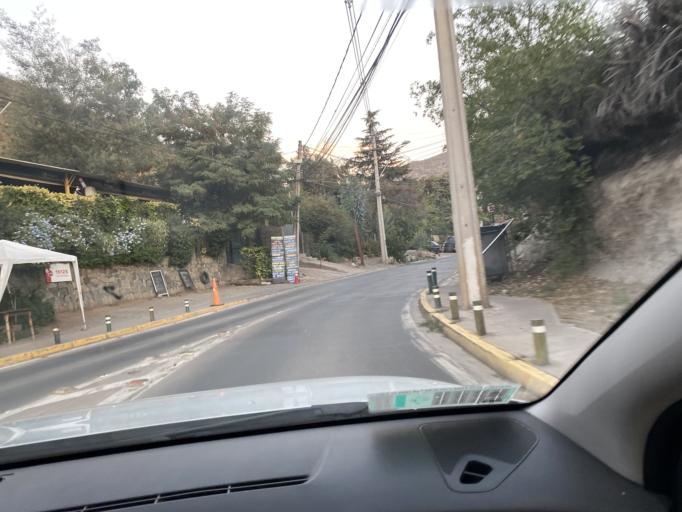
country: CL
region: Santiago Metropolitan
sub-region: Provincia de Santiago
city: Villa Presidente Frei, Nunoa, Santiago, Chile
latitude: -33.3612
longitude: -70.4923
